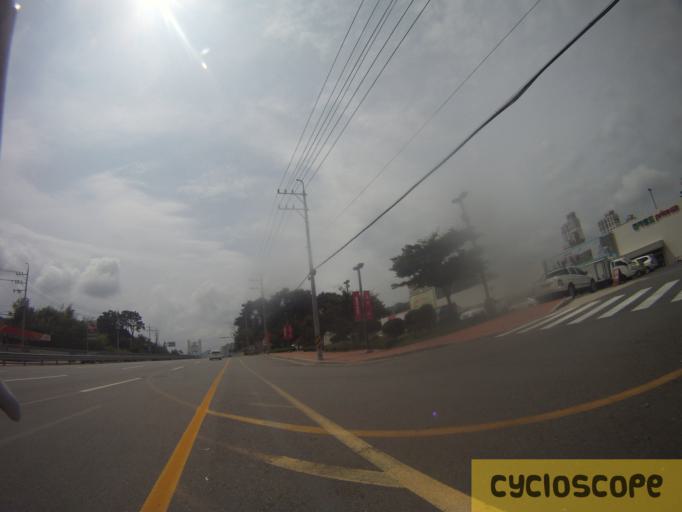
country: KR
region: Busan
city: Kijang
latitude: 35.2523
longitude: 129.2215
